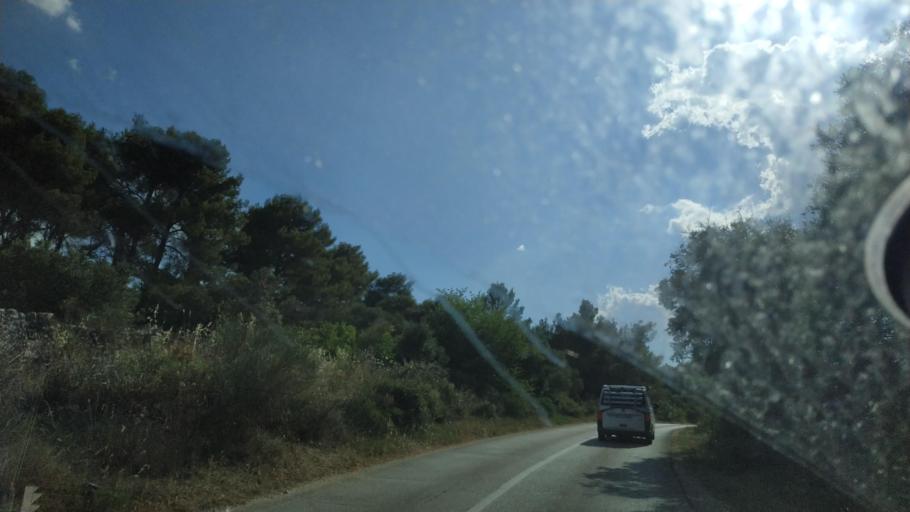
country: HR
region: Splitsko-Dalmatinska
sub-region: Grad Trogir
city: Trogir
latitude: 43.4885
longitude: 16.2505
